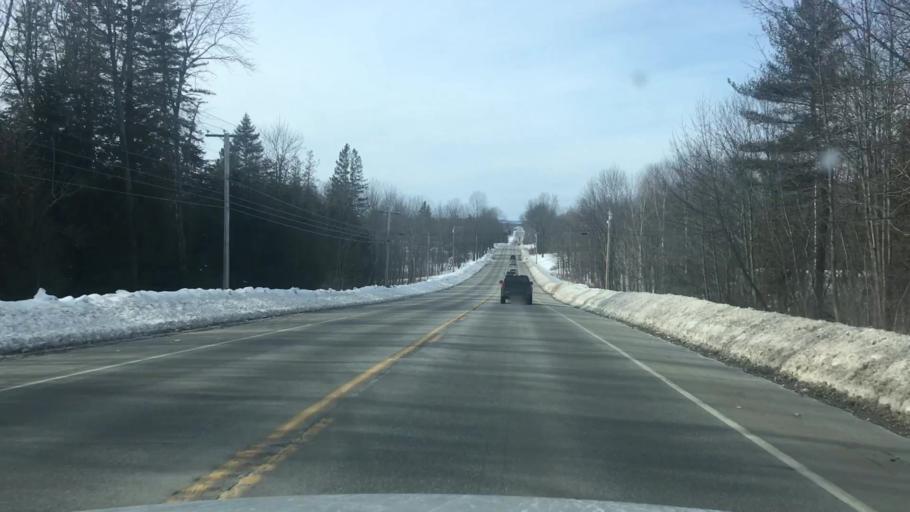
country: US
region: Maine
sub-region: Penobscot County
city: Kenduskeag
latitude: 44.9720
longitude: -68.9789
